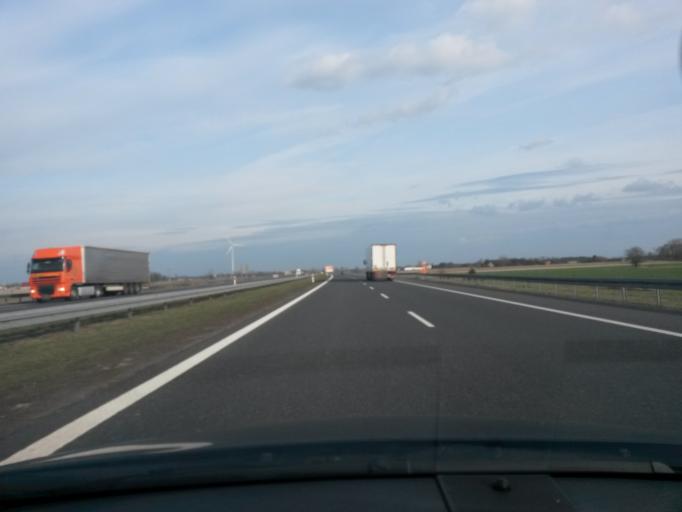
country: PL
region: Lodz Voivodeship
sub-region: Powiat leczycki
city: Swinice Warckie
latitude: 52.0166
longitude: 18.9443
